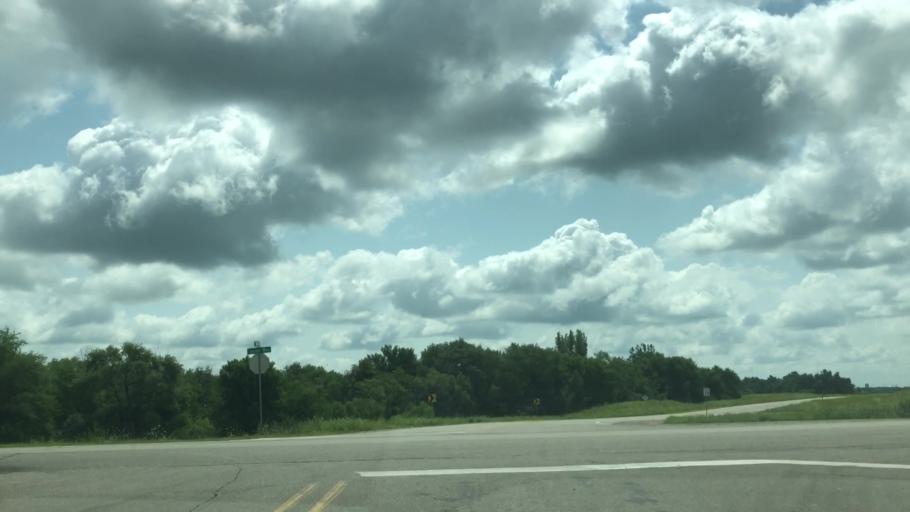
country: US
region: Iowa
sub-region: Marshall County
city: Marshalltown
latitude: 42.0335
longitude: -92.9606
